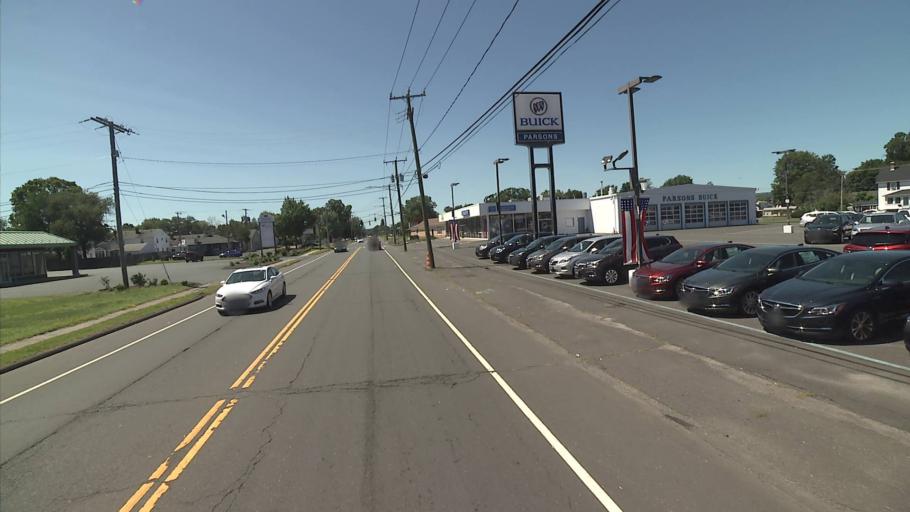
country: US
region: Connecticut
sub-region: Hartford County
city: Plainville
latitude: 41.6644
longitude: -72.8636
